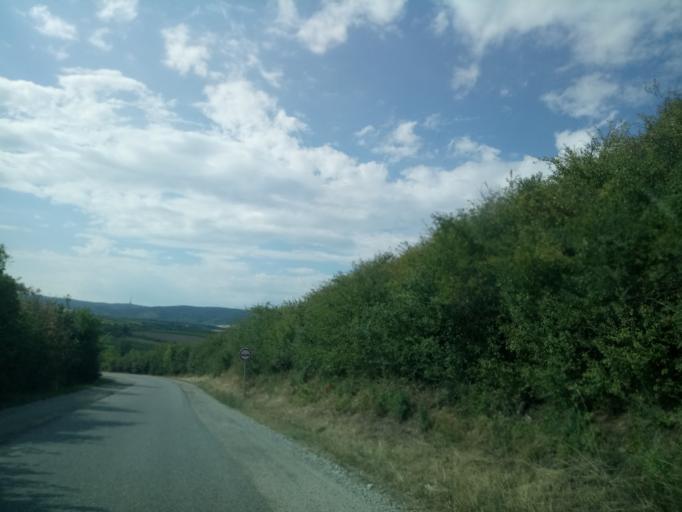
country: RS
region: Autonomna Pokrajina Vojvodina
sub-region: Sremski Okrug
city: Irig
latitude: 45.1058
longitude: 19.9169
